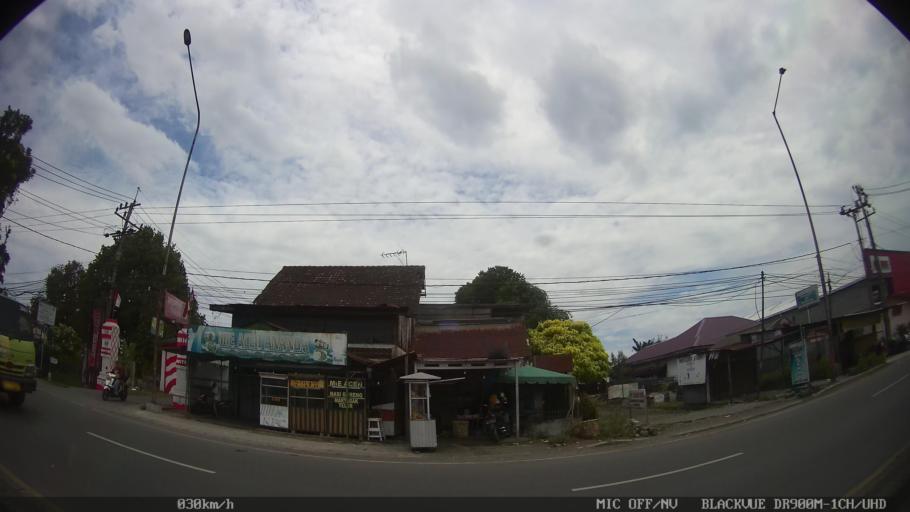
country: ID
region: North Sumatra
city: Sunggal
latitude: 3.5991
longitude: 98.5952
